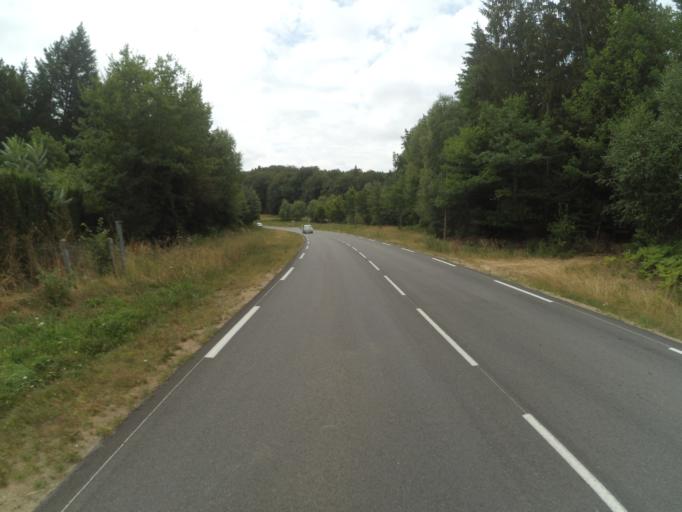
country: FR
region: Limousin
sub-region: Departement de la Correze
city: Ussel
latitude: 45.5853
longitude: 2.2906
